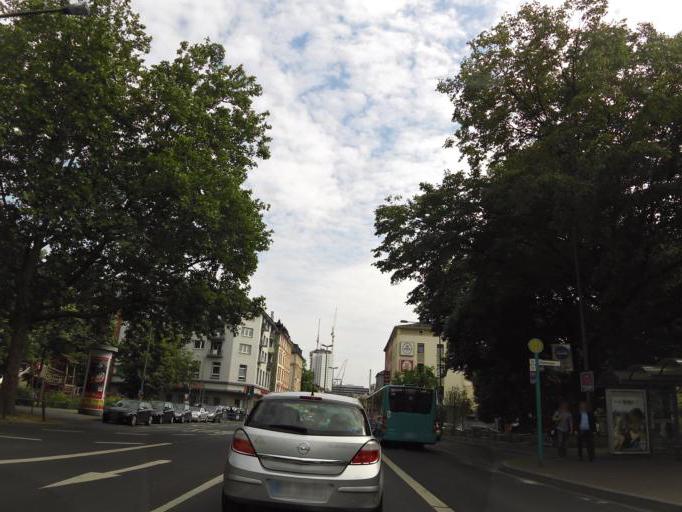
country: DE
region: Hesse
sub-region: Regierungsbezirk Darmstadt
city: Frankfurt am Main
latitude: 50.1047
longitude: 8.6898
